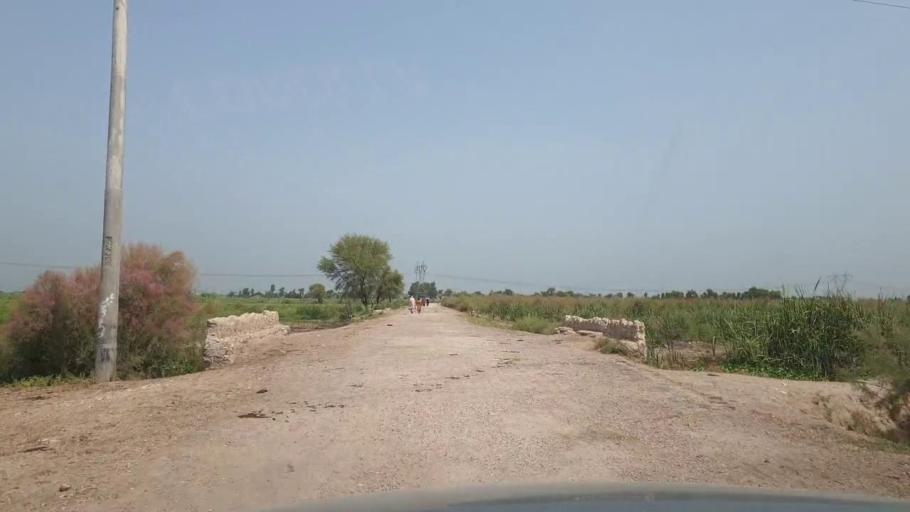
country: PK
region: Sindh
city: Madeji
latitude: 27.8011
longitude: 68.5208
